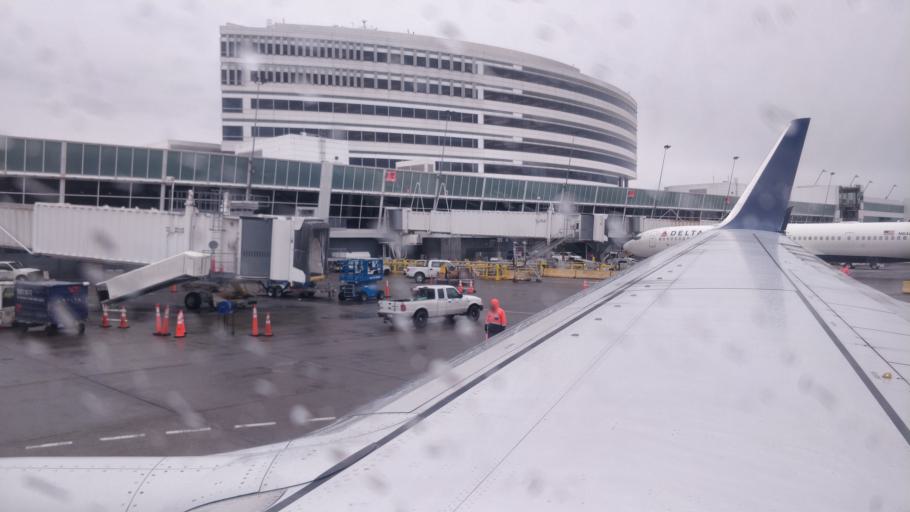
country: US
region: Washington
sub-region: King County
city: SeaTac
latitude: 47.4418
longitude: -122.3025
